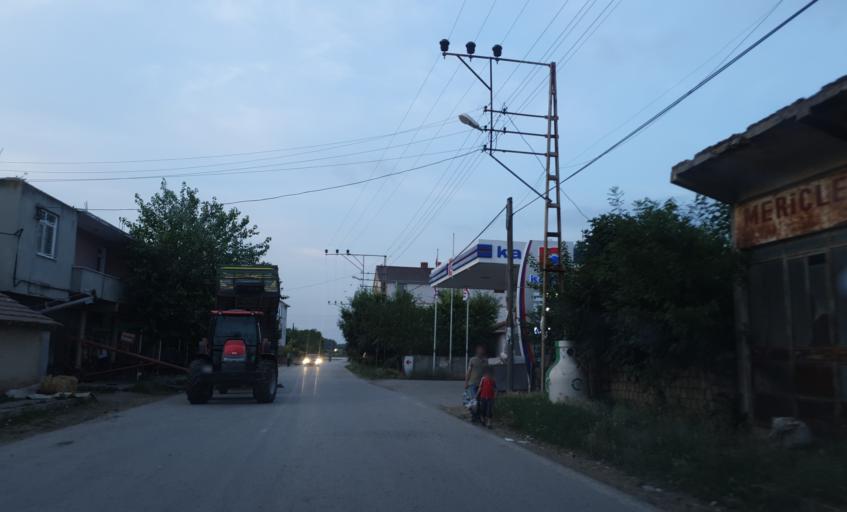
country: TR
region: Tekirdag
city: Beyazkoy
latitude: 41.3857
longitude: 27.6208
